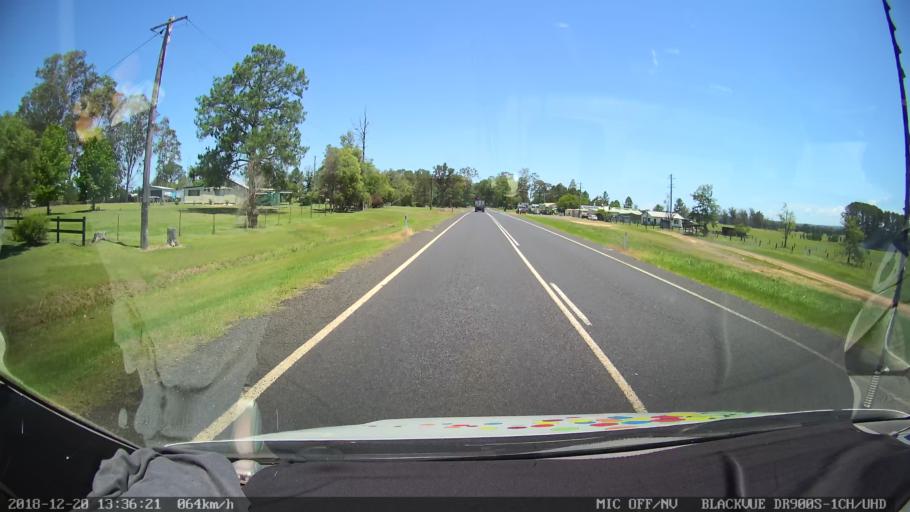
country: AU
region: New South Wales
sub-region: Clarence Valley
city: Maclean
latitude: -29.2809
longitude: 152.9900
